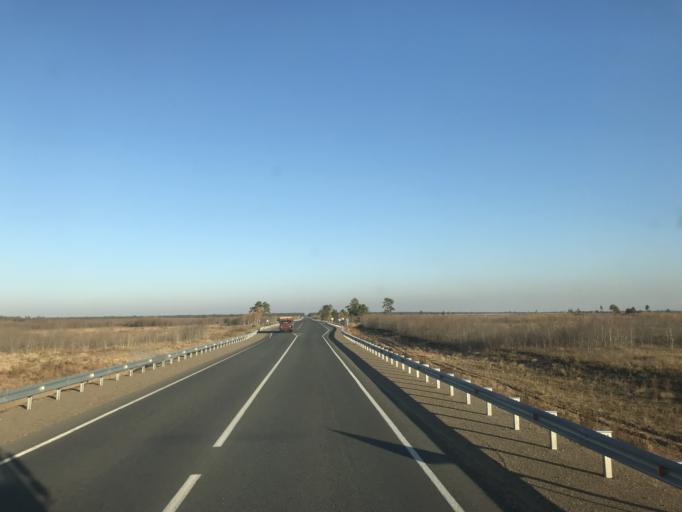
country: KZ
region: Pavlodar
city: Kurchatov
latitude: 51.1034
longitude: 78.9919
